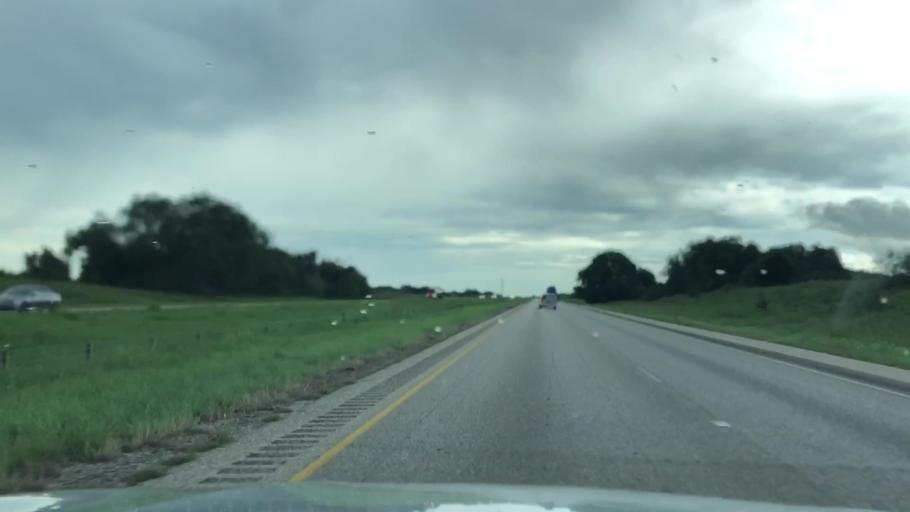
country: US
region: Texas
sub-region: Fayette County
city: Flatonia
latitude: 29.6961
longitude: -97.0350
